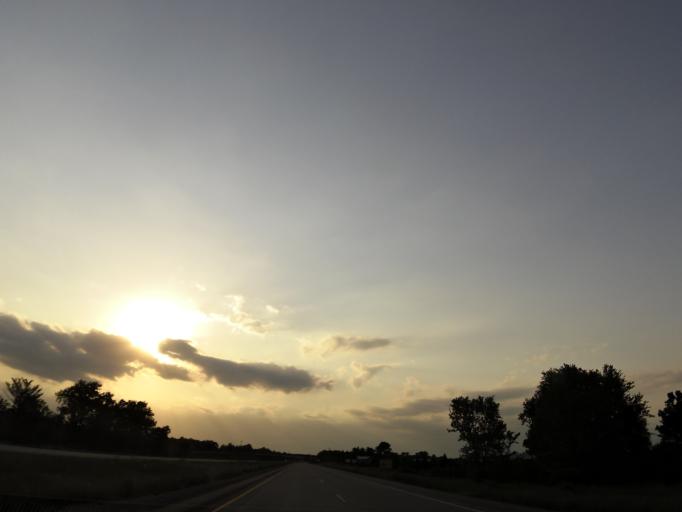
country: US
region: Wisconsin
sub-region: Jackson County
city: Black River Falls
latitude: 44.3593
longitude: -90.9590
